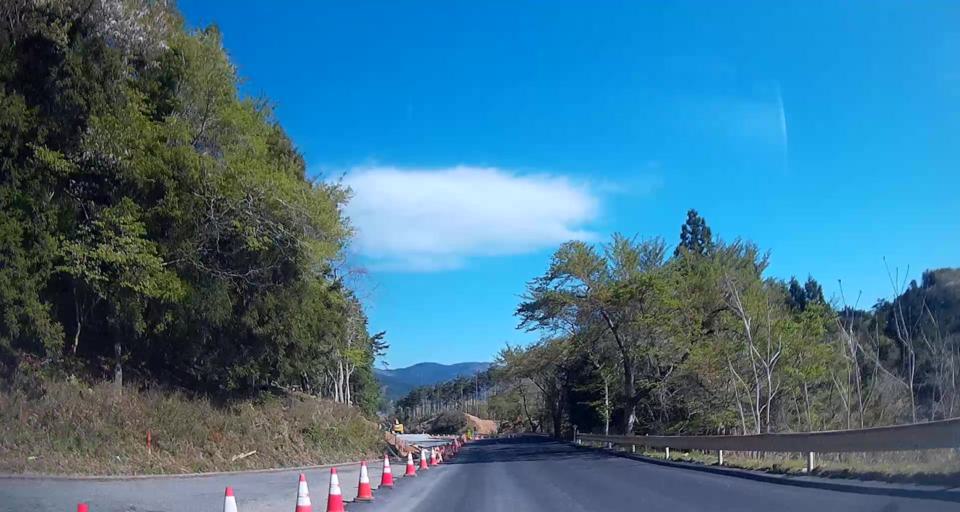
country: JP
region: Miyagi
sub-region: Oshika Gun
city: Onagawa Cho
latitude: 38.4340
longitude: 141.4470
